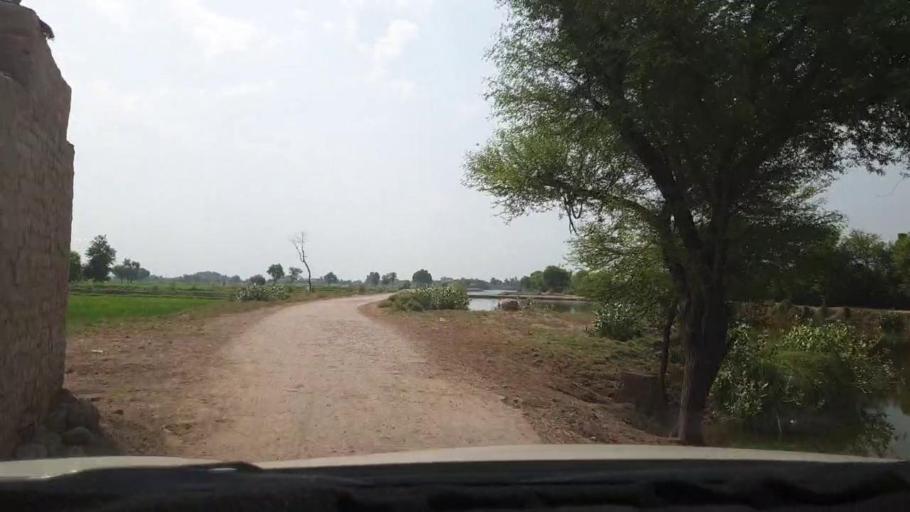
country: PK
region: Sindh
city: Dokri
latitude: 27.3862
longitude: 68.1231
